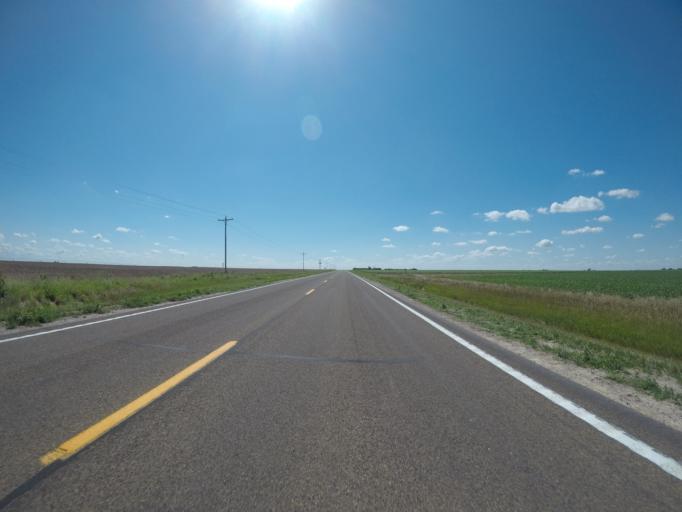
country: US
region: Nebraska
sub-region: Chase County
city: Imperial
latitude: 40.5376
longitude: -101.7494
